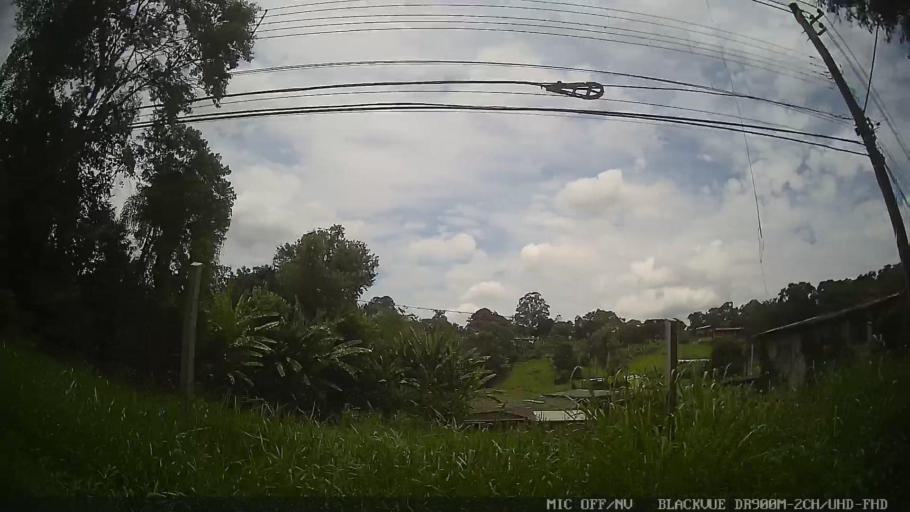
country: BR
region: Sao Paulo
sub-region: Santa Isabel
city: Santa Isabel
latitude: -23.3595
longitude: -46.2345
